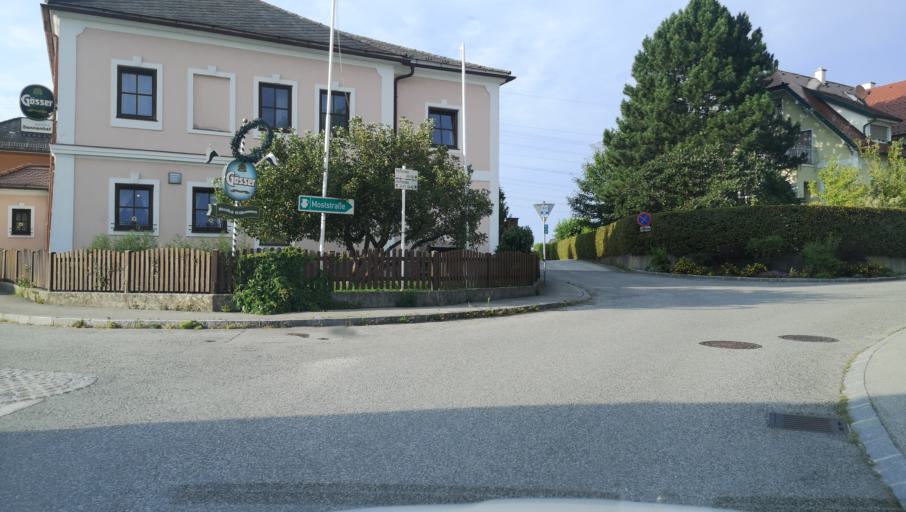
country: AT
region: Lower Austria
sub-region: Politischer Bezirk Amstetten
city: Amstetten
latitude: 48.1515
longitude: 14.8945
